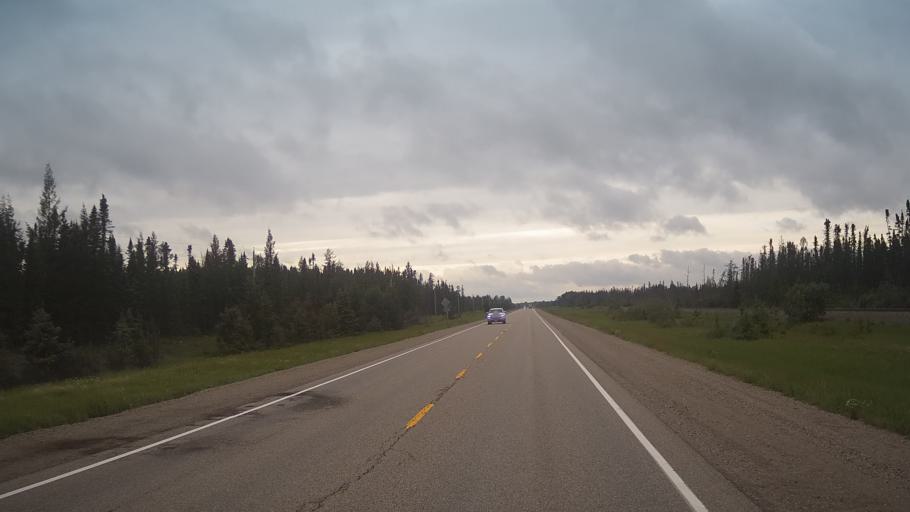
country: CA
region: Ontario
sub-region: Thunder Bay District
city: Thunder Bay
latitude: 48.8602
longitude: -89.9629
